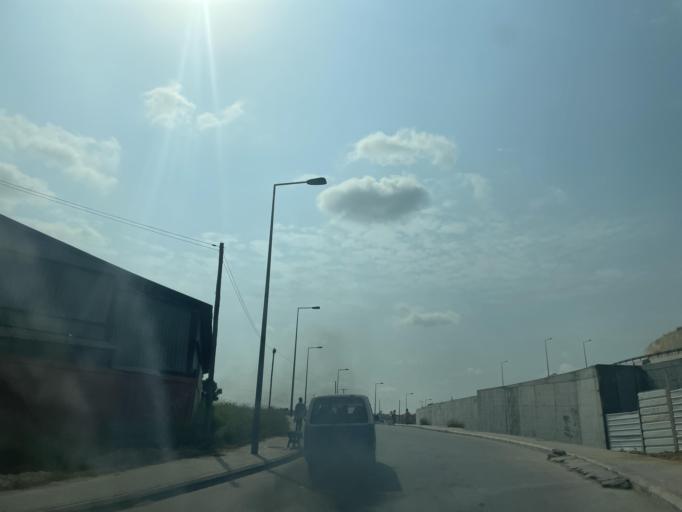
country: AO
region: Luanda
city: Luanda
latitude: -8.8041
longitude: 13.2504
